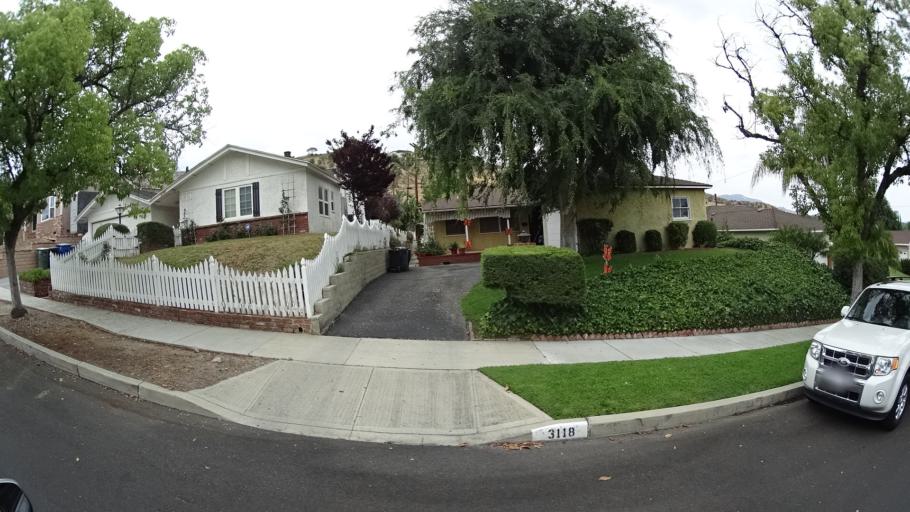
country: US
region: California
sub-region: Los Angeles County
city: Burbank
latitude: 34.2073
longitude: -118.3293
